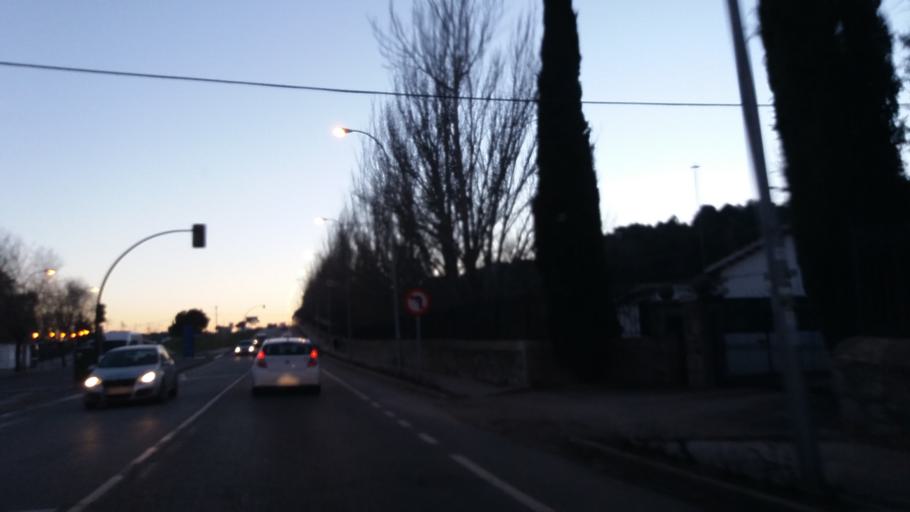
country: ES
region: Madrid
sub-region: Provincia de Madrid
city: Guadarrama
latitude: 40.6671
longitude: -4.0888
